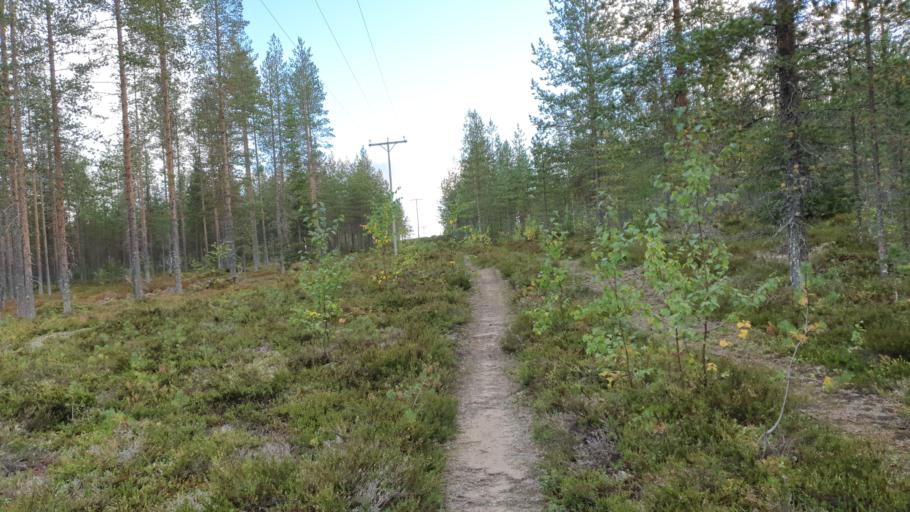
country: FI
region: Kainuu
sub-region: Kehys-Kainuu
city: Kuhmo
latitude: 64.2009
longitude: 29.1612
